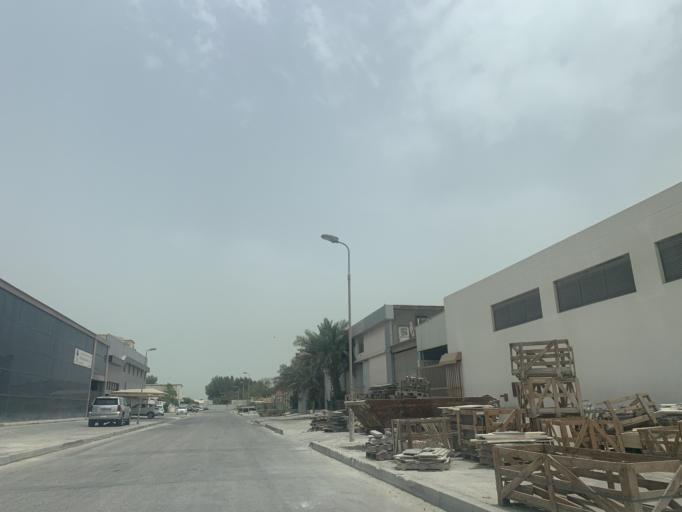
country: BH
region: Northern
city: Sitrah
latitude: 26.1742
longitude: 50.6014
